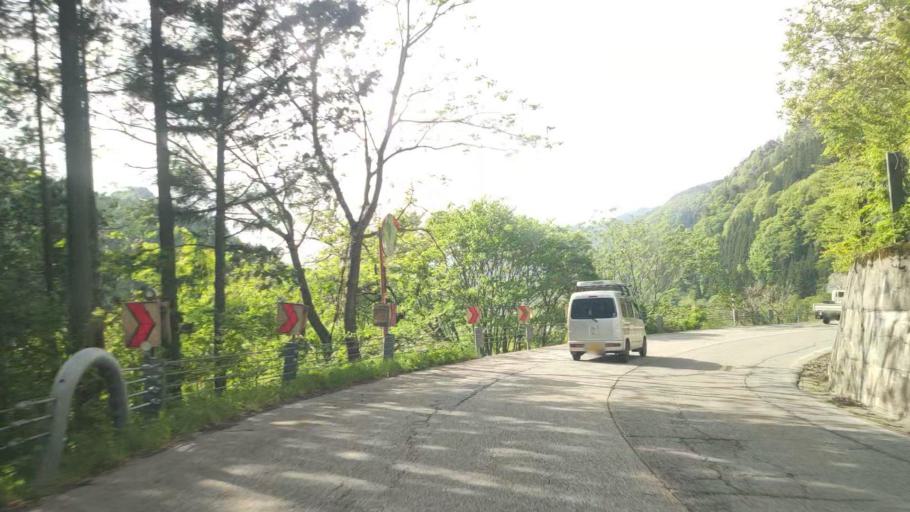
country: JP
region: Gifu
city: Takayama
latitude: 36.2712
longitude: 137.3927
